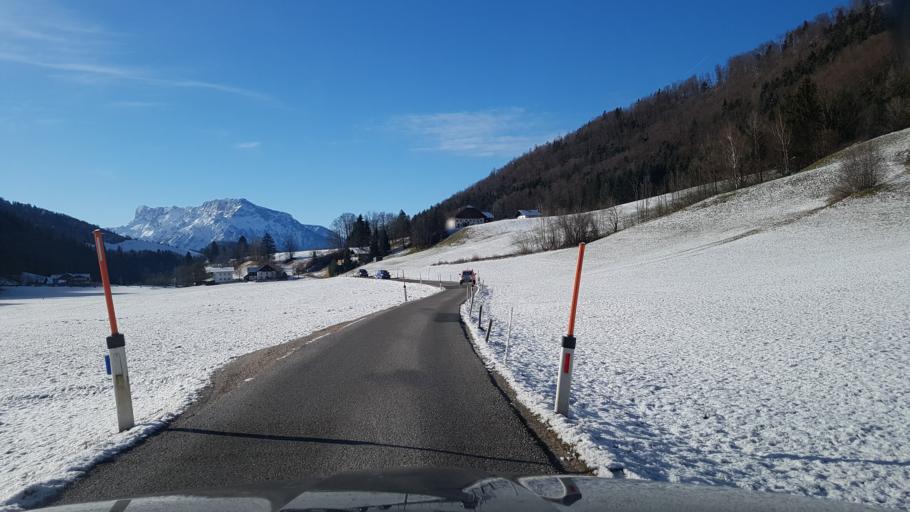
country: AT
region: Salzburg
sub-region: Politischer Bezirk Salzburg-Umgebung
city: Koppl
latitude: 47.7778
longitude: 13.1425
